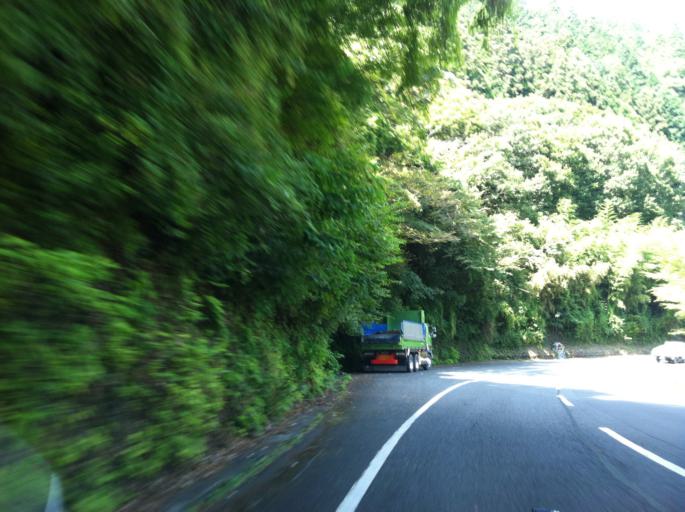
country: JP
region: Shizuoka
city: Shizuoka-shi
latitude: 35.0664
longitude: 138.2426
